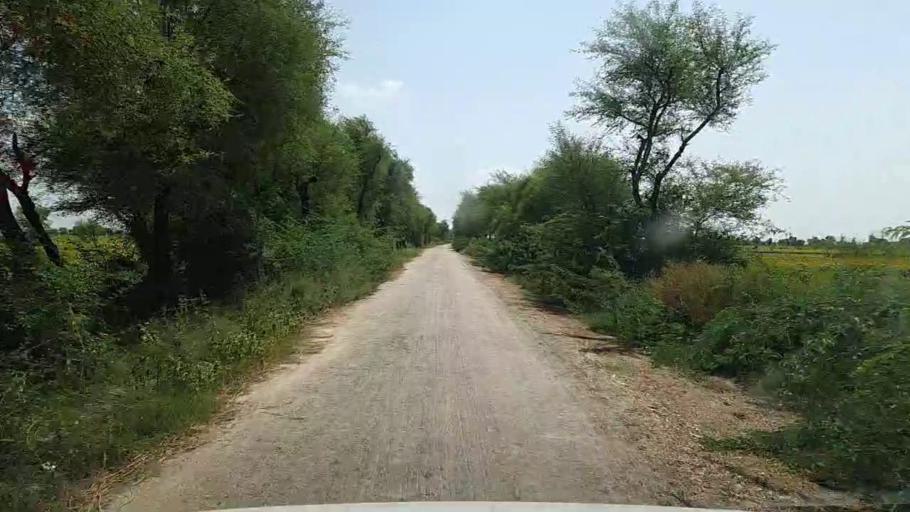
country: PK
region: Sindh
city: Kario
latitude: 24.6513
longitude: 68.5640
